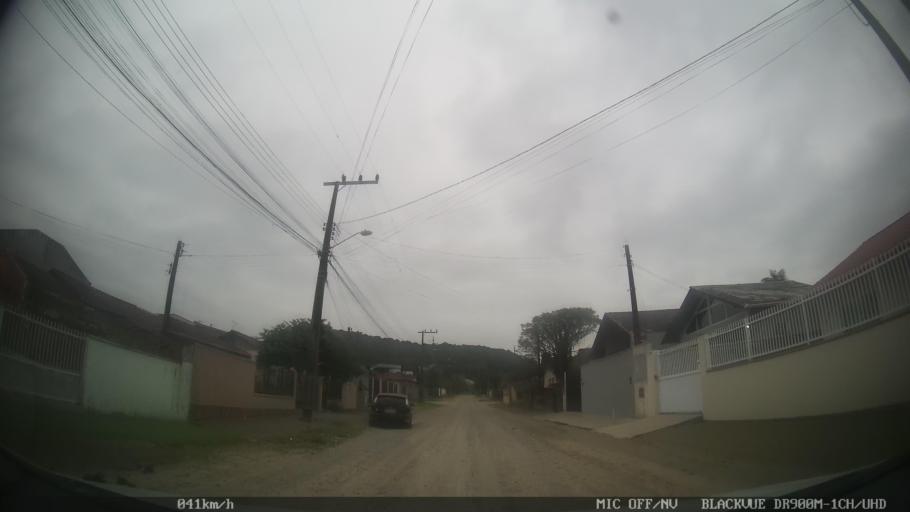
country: BR
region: Santa Catarina
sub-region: Joinville
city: Joinville
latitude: -26.3693
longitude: -48.8303
